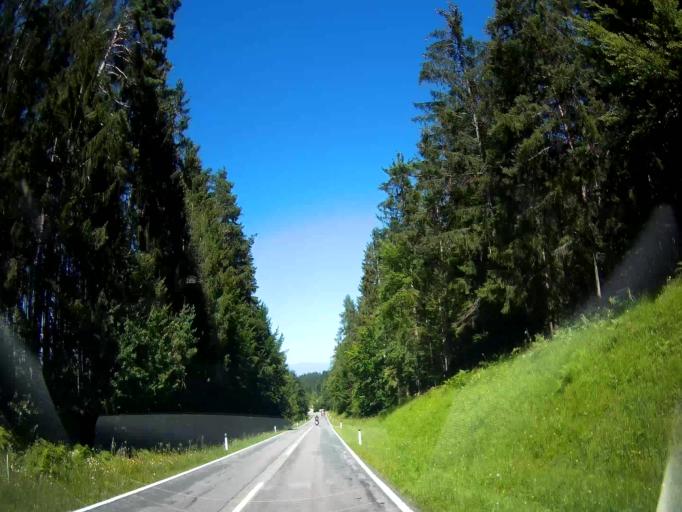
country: AT
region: Carinthia
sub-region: Politischer Bezirk Volkermarkt
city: Gallizien
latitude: 46.5384
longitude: 14.4711
